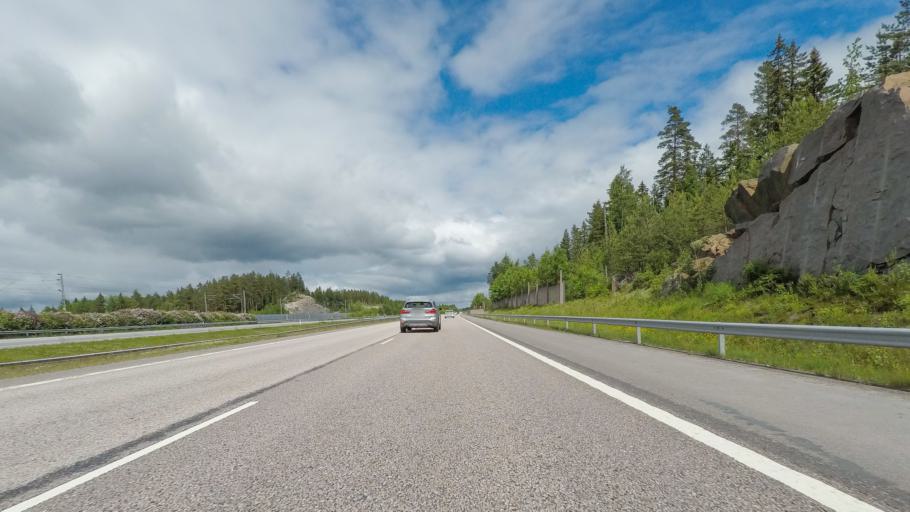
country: FI
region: Uusimaa
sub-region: Porvoo
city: Pukkila
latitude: 60.7293
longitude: 25.4443
